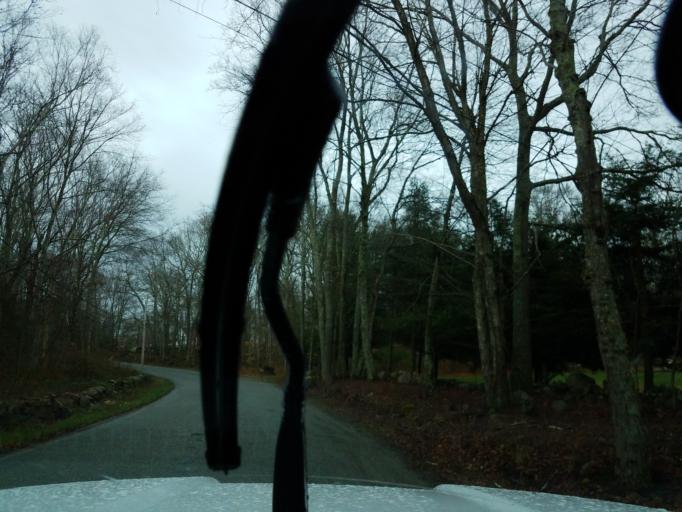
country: US
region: Rhode Island
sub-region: Washington County
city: Ashaway
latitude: 41.4469
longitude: -71.8227
